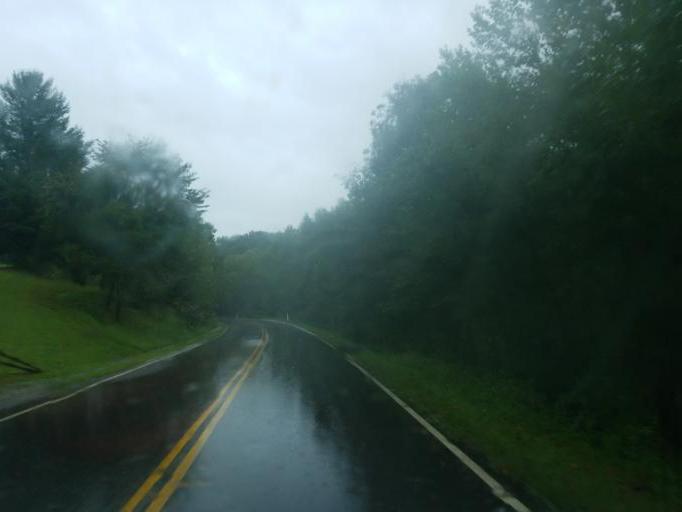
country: US
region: Kentucky
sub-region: Carter County
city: Grayson
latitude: 38.4971
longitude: -82.9993
